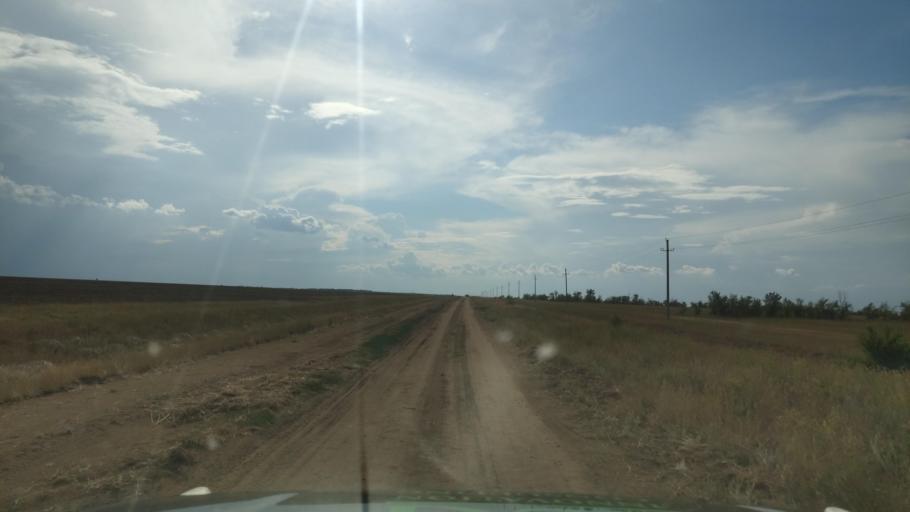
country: KZ
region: Pavlodar
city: Pavlodar
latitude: 52.5129
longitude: 77.4803
